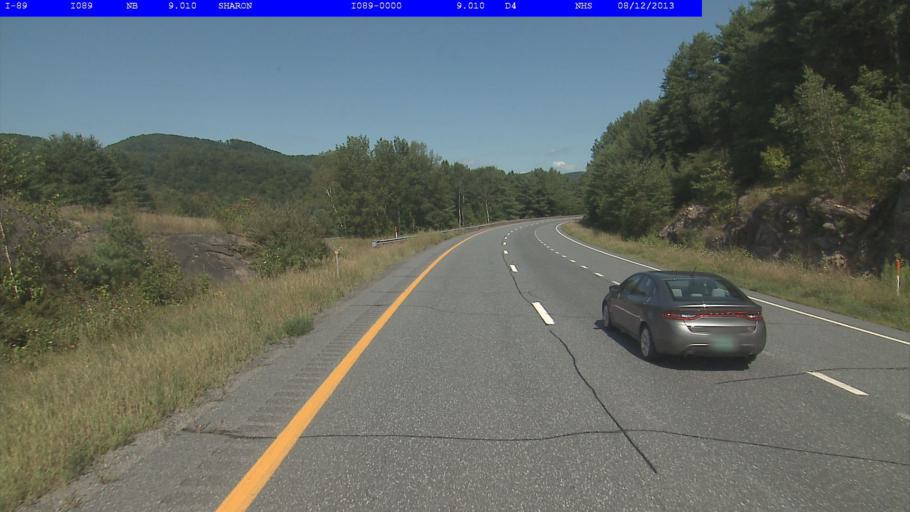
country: US
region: Vermont
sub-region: Windsor County
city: Wilder
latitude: 43.7284
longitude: -72.4296
